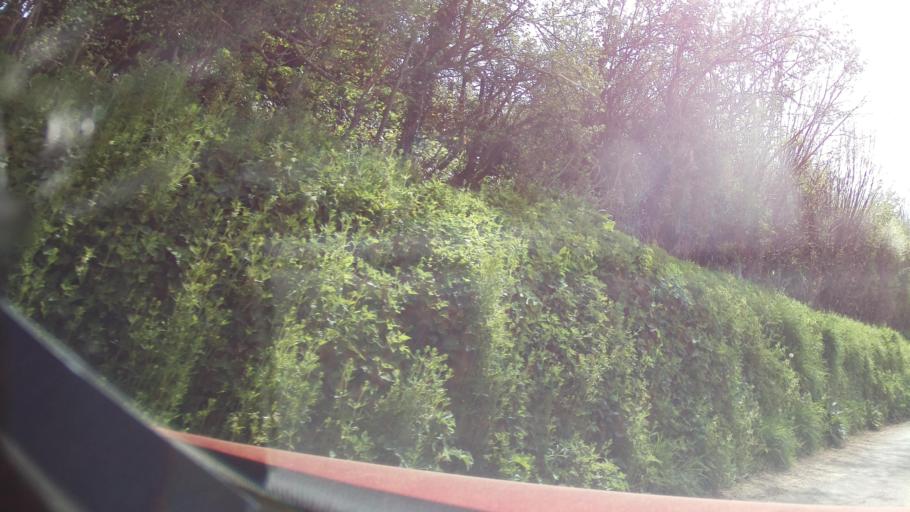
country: GB
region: England
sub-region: Dorset
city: Sherborne
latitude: 50.9865
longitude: -2.5391
